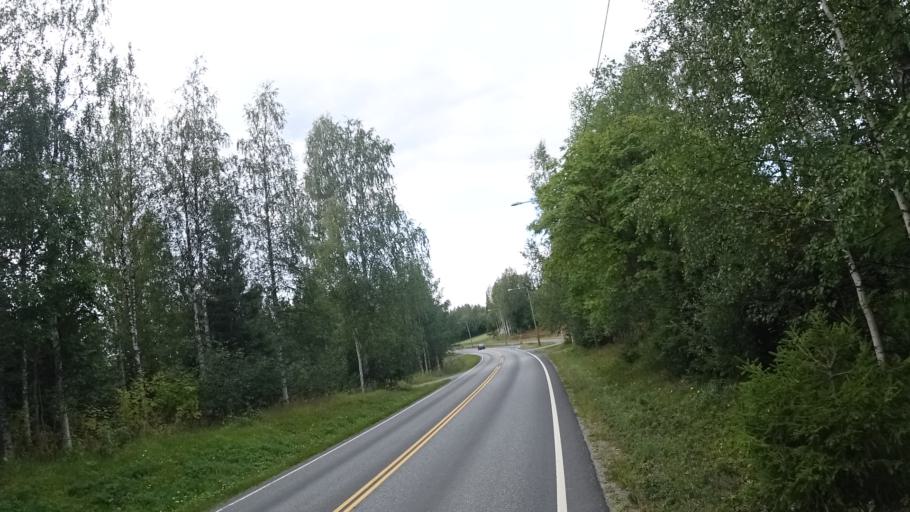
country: FI
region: North Karelia
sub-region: Joensuu
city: Ilomantsi
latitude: 62.6522
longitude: 30.9695
